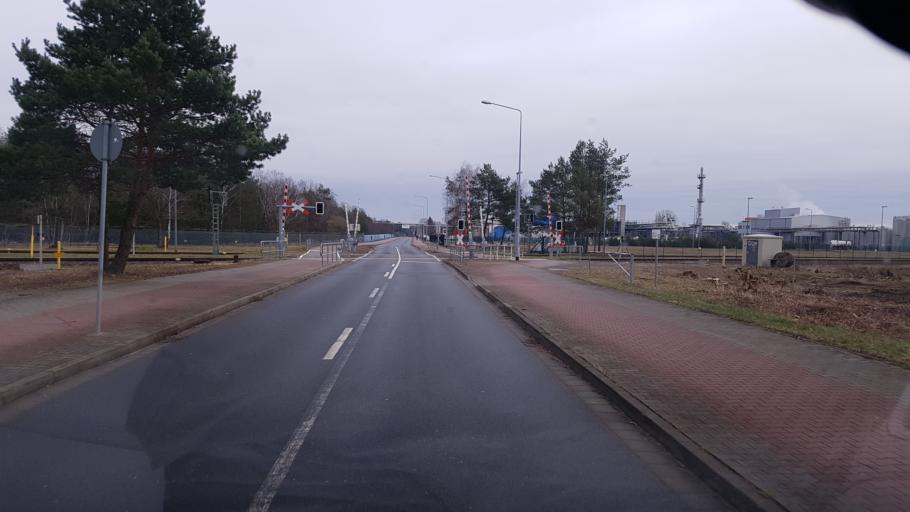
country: DE
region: Brandenburg
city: Ruhland
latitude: 51.4721
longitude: 13.8762
